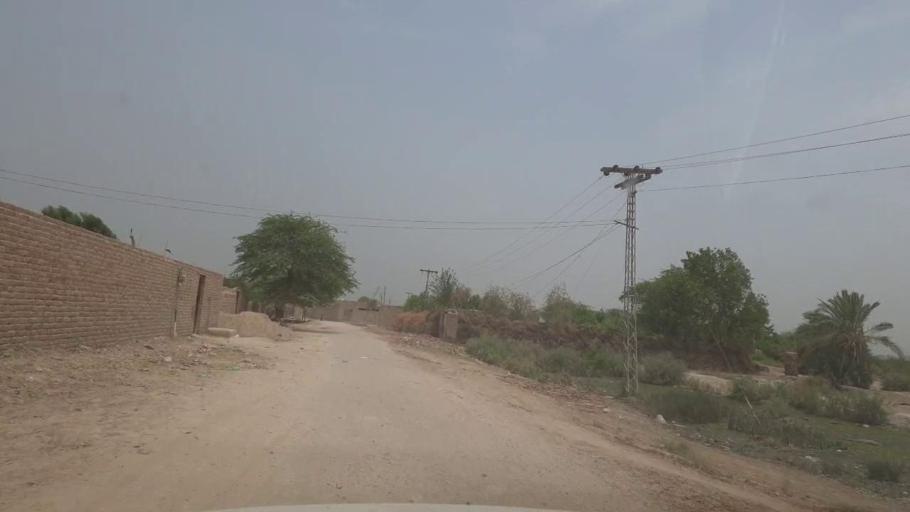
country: PK
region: Sindh
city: Kot Diji
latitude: 27.4358
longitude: 68.6440
